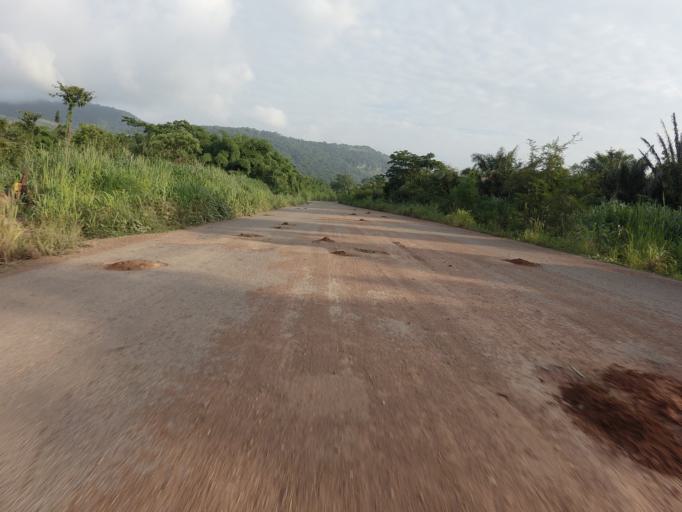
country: TG
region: Plateaux
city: Kpalime
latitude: 6.9331
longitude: 0.4628
